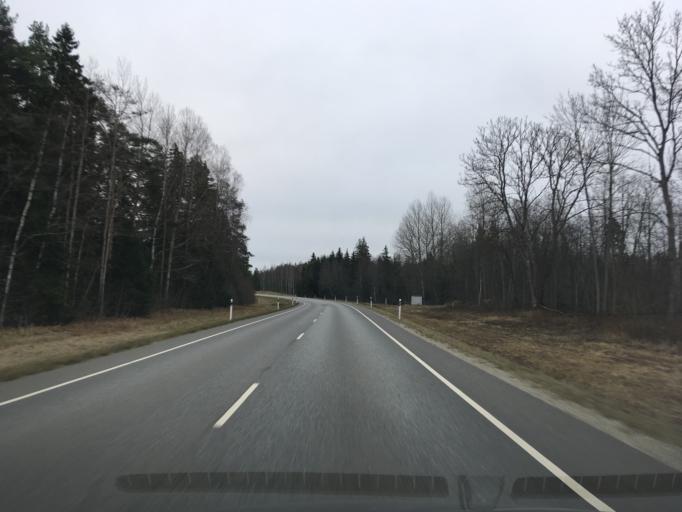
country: EE
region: Laeaene-Virumaa
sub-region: Kadrina vald
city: Kadrina
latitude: 59.4486
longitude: 26.0624
